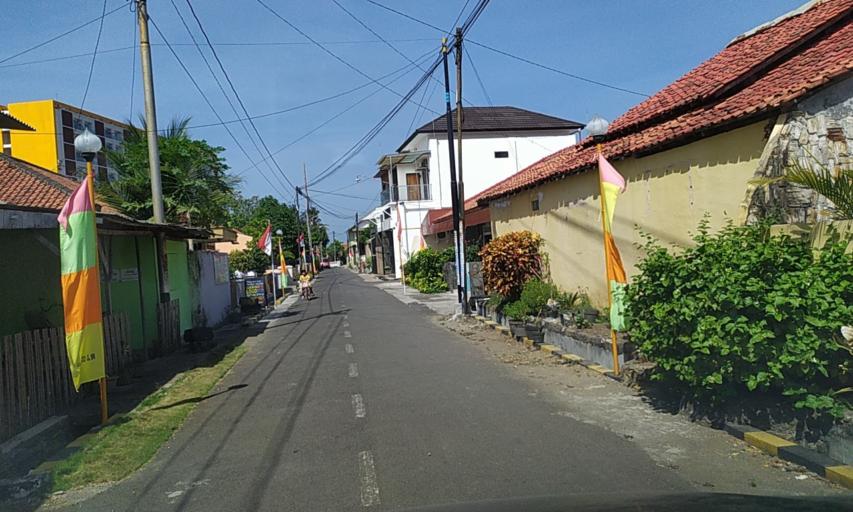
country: ID
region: Central Java
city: Karangbadar Kidul
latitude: -7.7138
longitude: 109.0069
